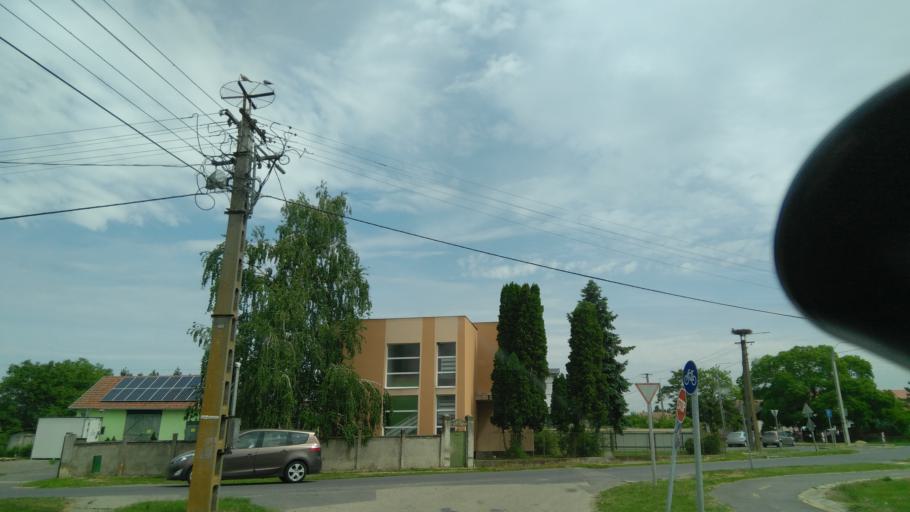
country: HU
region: Bekes
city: Fuzesgyarmat
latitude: 47.1094
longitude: 21.2090
